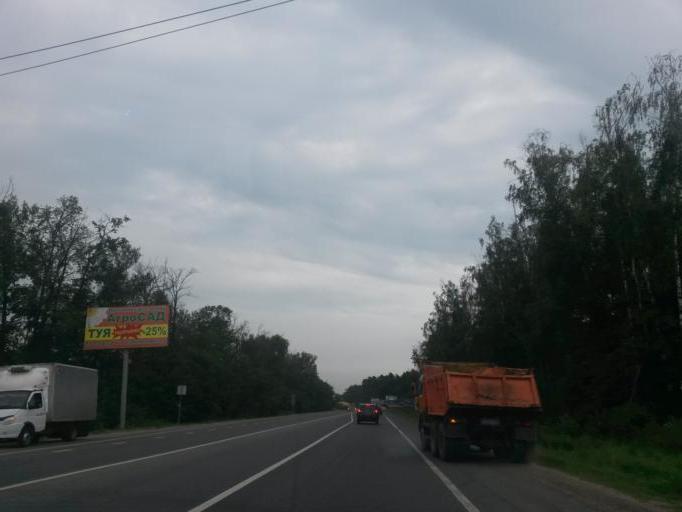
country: RU
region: Moskovskaya
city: Petrovskaya
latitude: 55.5347
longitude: 37.7688
